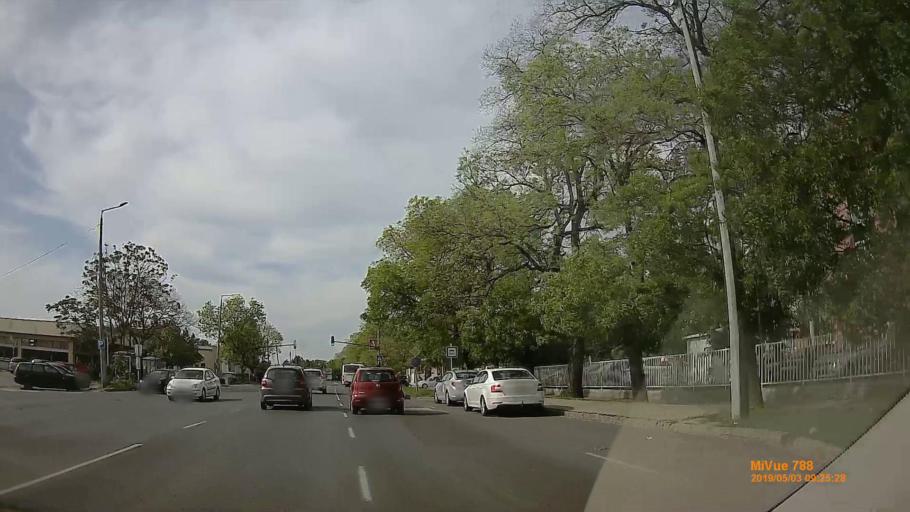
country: HU
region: Jasz-Nagykun-Szolnok
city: Szolnok
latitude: 47.1575
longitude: 20.1723
